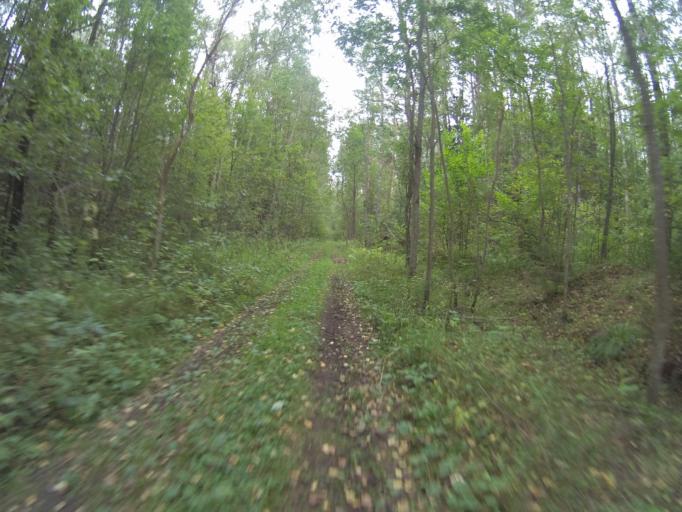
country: RU
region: Vladimir
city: Golovino
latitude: 56.0176
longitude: 40.4783
